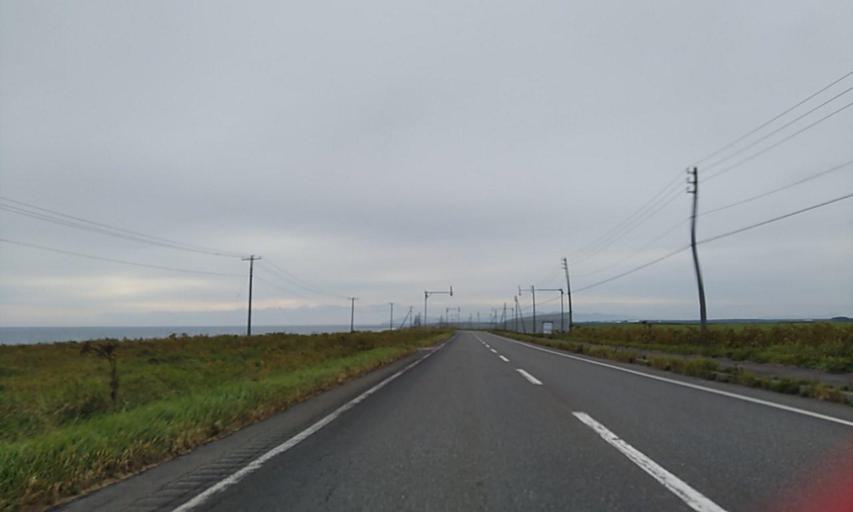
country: JP
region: Hokkaido
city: Makubetsu
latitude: 45.3208
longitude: 142.1850
